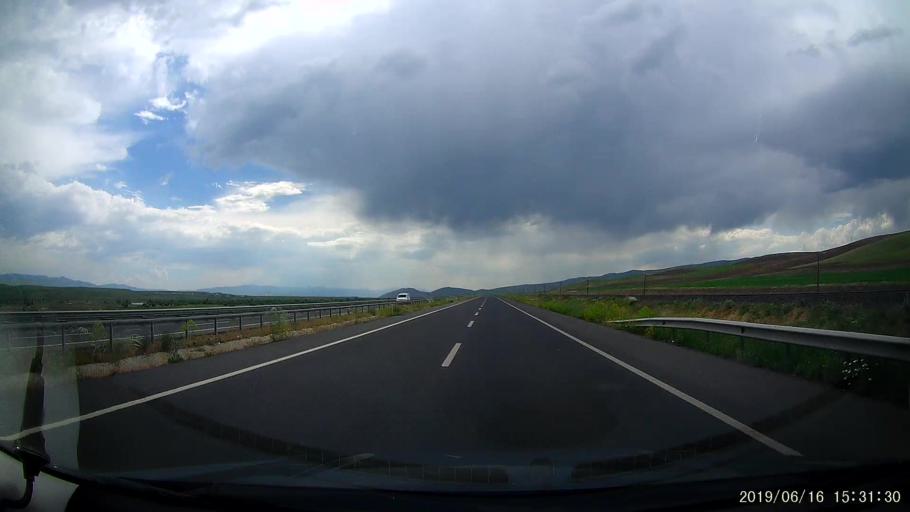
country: TR
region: Erzurum
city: Horasan
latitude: 40.0323
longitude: 42.0768
